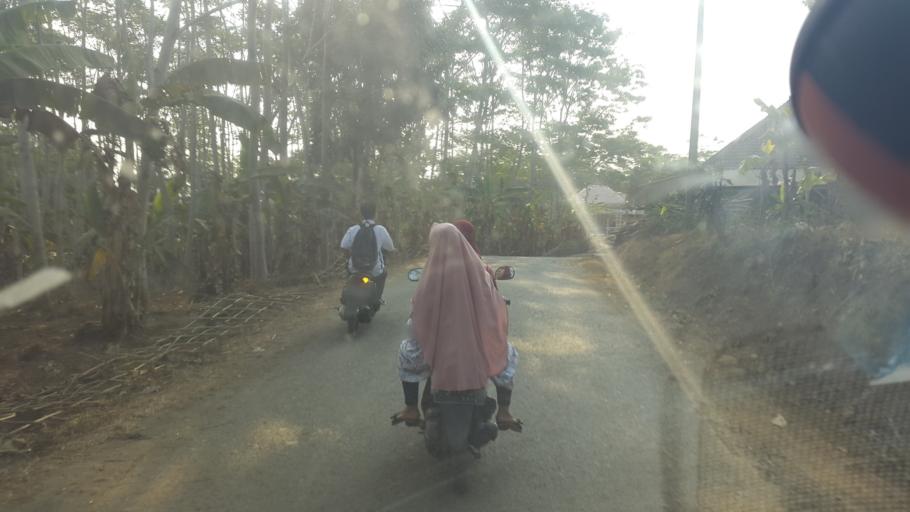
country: ID
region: West Java
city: Nagrak
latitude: -7.3360
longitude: 106.5558
